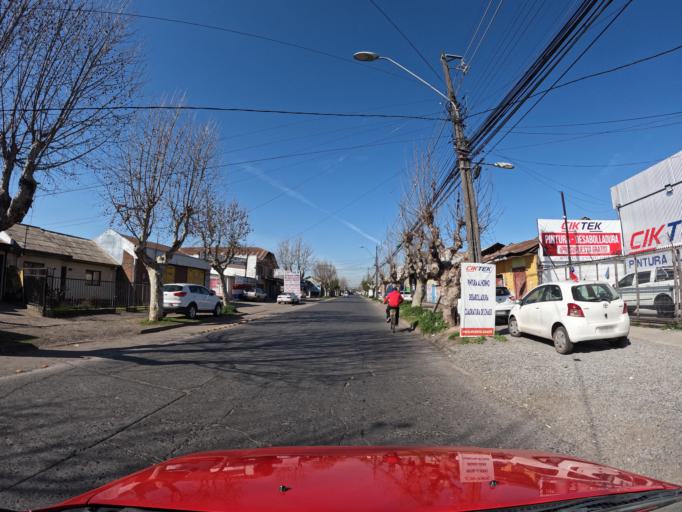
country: CL
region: Maule
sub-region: Provincia de Curico
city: Curico
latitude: -34.9790
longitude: -71.2450
